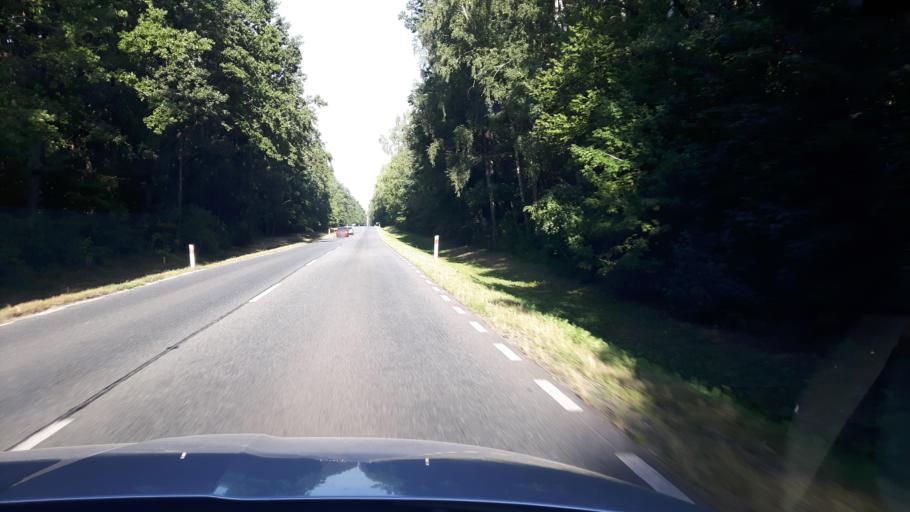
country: PL
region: Masovian Voivodeship
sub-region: Powiat legionowski
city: Wieliszew
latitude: 52.5018
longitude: 20.9479
